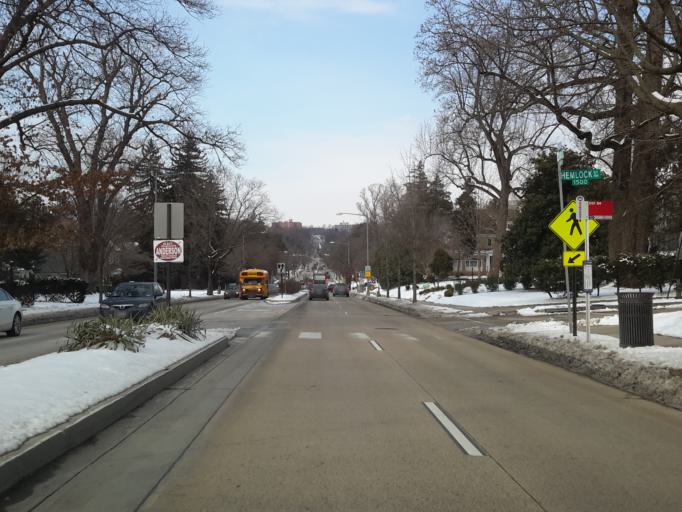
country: US
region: Maryland
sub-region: Montgomery County
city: Silver Spring
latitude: 38.9811
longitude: -77.0363
